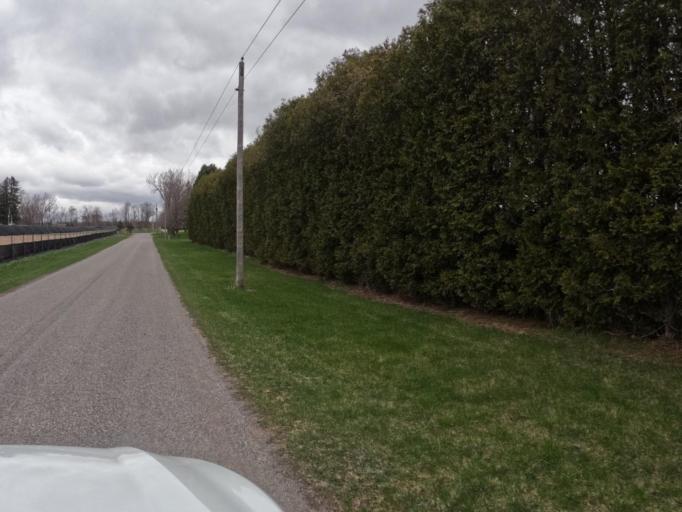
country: CA
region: Ontario
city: Norfolk County
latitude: 42.9629
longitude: -80.4278
